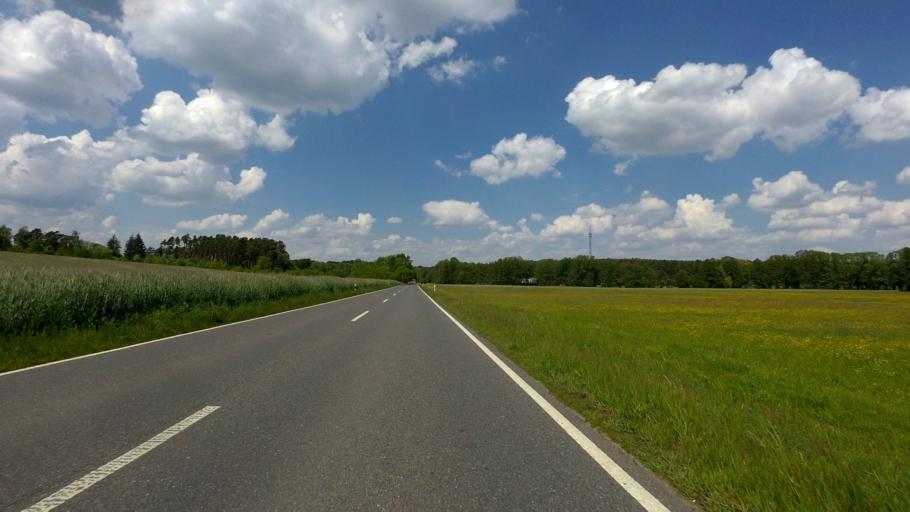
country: DE
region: Brandenburg
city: Lieberose
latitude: 51.9868
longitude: 14.2133
